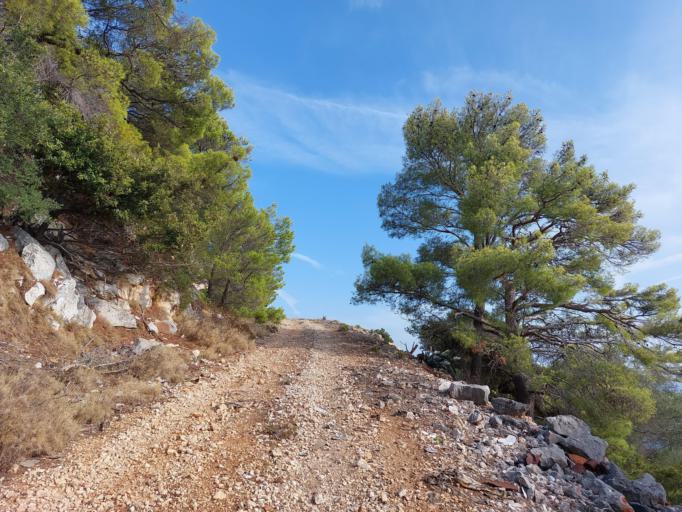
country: HR
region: Dubrovacko-Neretvanska
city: Smokvica
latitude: 42.7330
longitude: 16.8297
